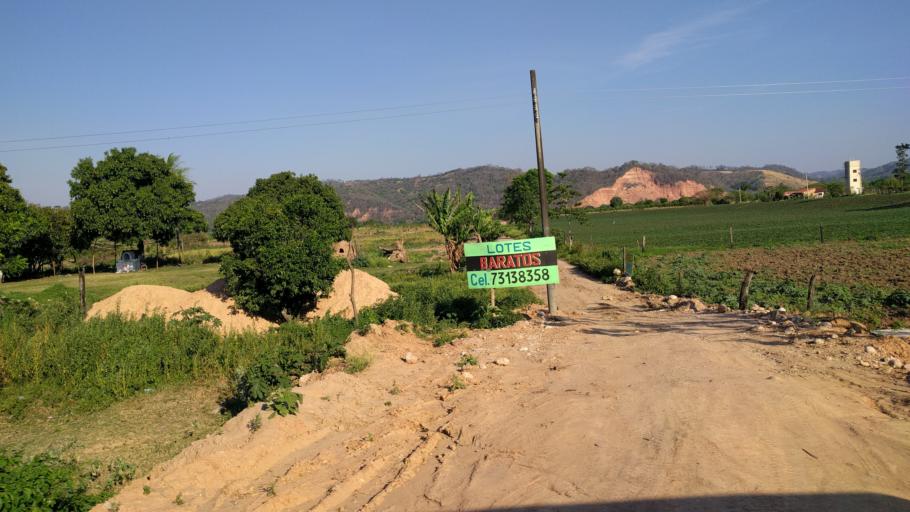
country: BO
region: Santa Cruz
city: Jorochito
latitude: -18.1392
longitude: -63.4774
